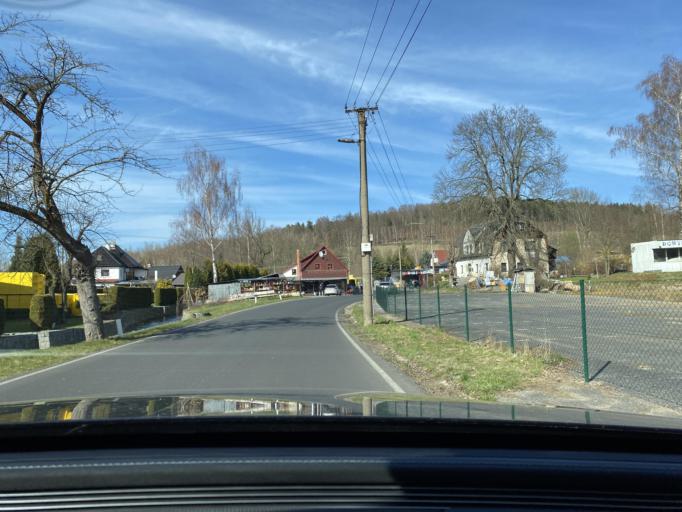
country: CZ
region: Ustecky
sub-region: Okres Decin
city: Sluknov
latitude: 51.0299
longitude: 14.4513
